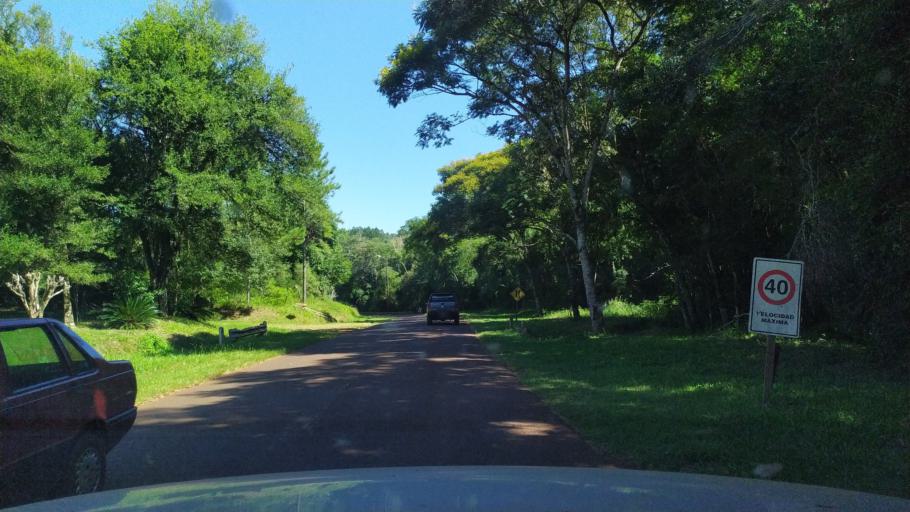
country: AR
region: Misiones
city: Caraguatay
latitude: -26.6547
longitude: -54.7407
